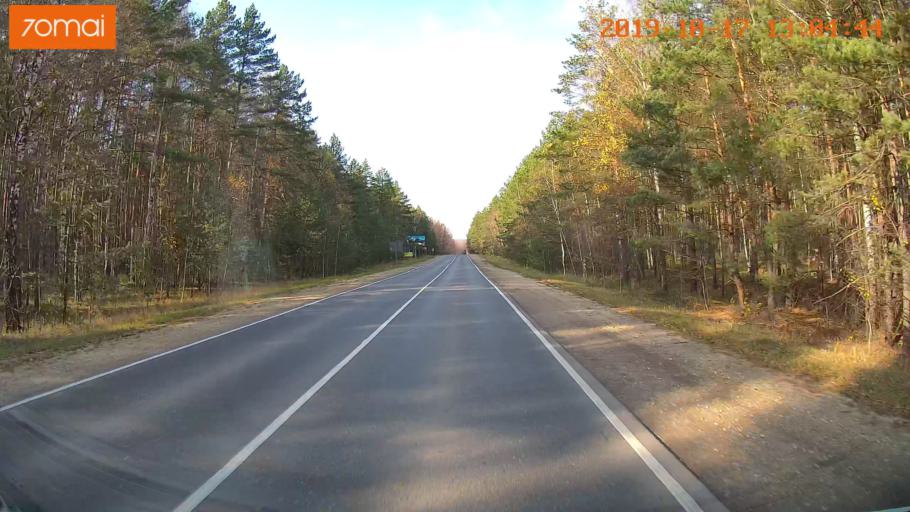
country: RU
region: Rjazan
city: Syntul
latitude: 54.9647
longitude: 41.3393
